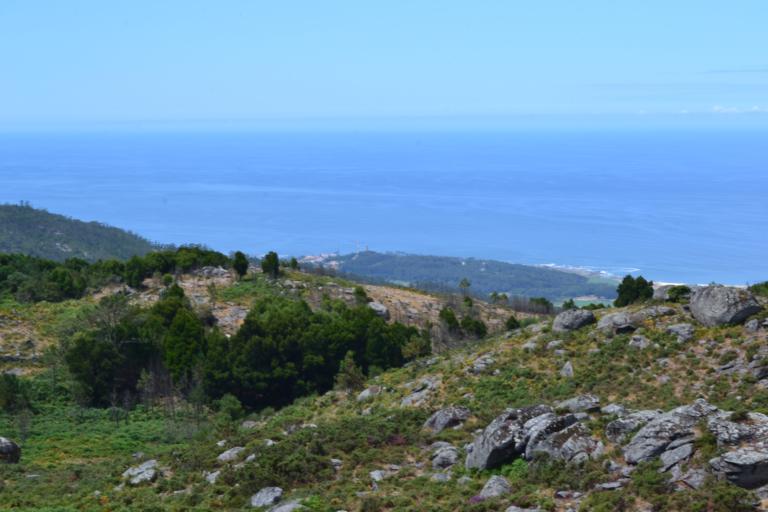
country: PT
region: Viana do Castelo
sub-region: Caminha
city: Vila Praia de Ancora
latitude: 41.7764
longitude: -8.8247
